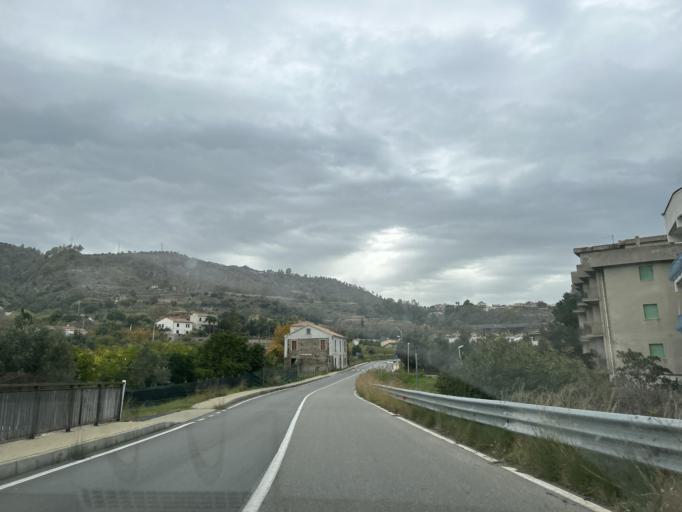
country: IT
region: Calabria
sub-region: Provincia di Catanzaro
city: Montepaone Lido
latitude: 38.7399
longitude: 16.5488
